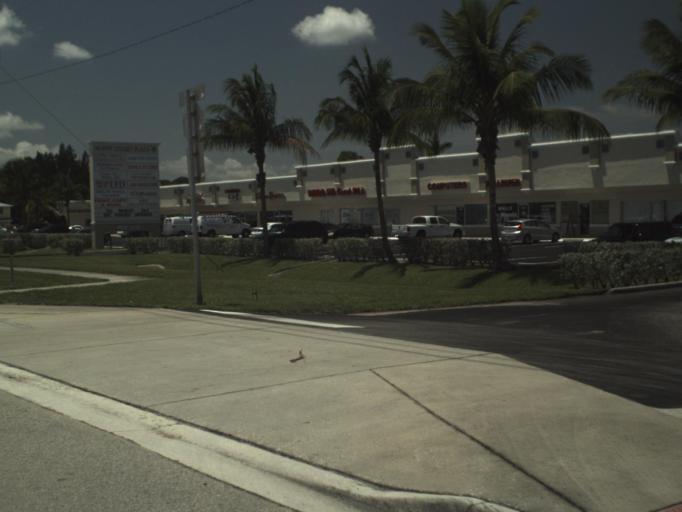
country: US
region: Florida
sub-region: Martin County
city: North River Shores
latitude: 27.2259
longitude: -80.2650
